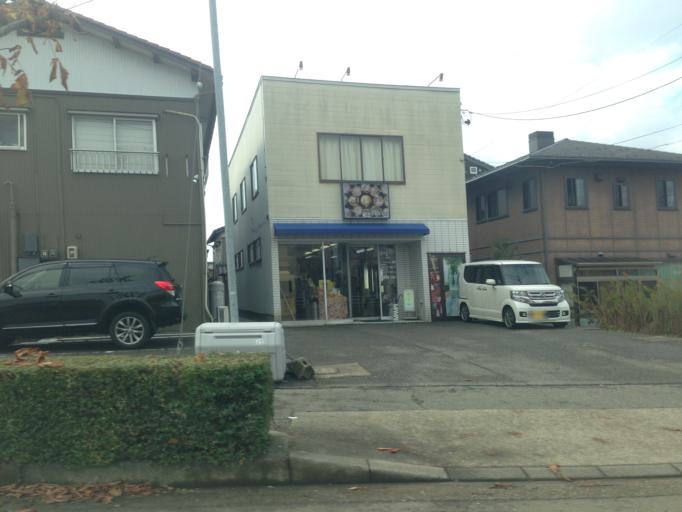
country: JP
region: Ishikawa
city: Komatsu
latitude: 36.2950
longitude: 136.3597
